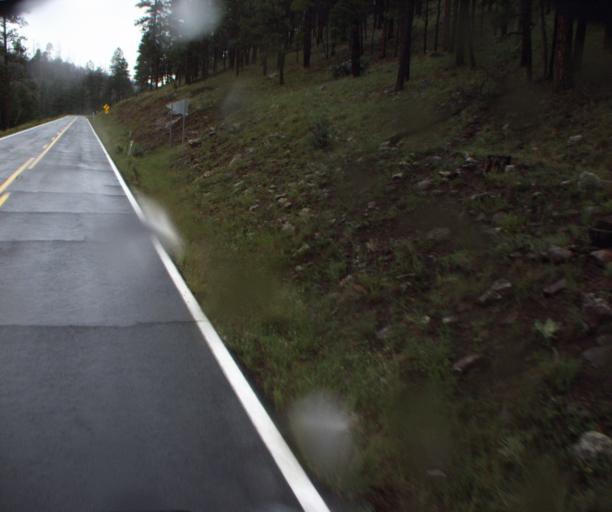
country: US
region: Arizona
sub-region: Apache County
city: Eagar
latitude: 33.7473
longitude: -109.2077
